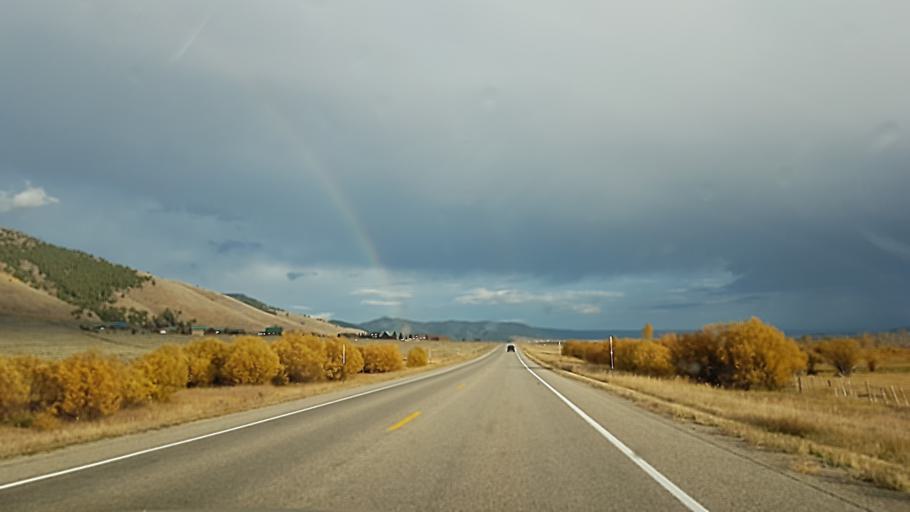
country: US
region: Montana
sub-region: Gallatin County
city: West Yellowstone
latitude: 44.6837
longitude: -111.4331
